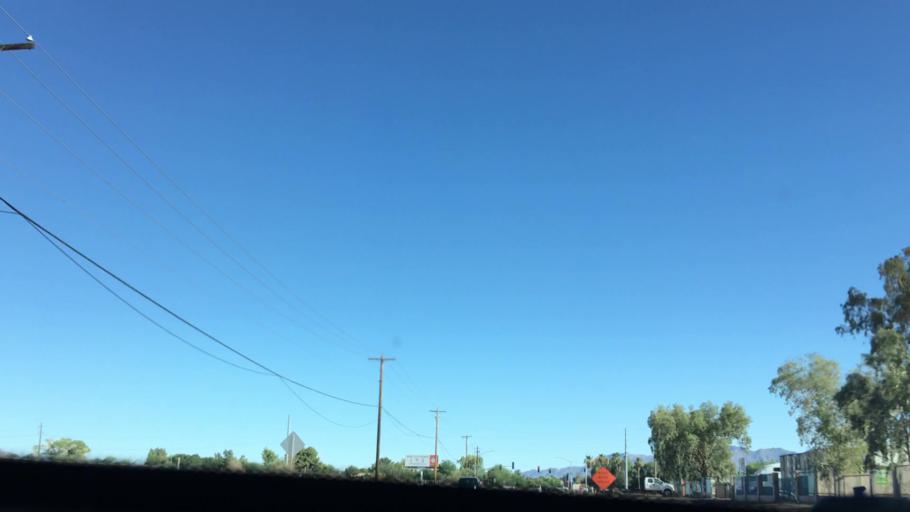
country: US
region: Arizona
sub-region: Maricopa County
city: Laveen
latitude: 33.3944
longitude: -112.2032
